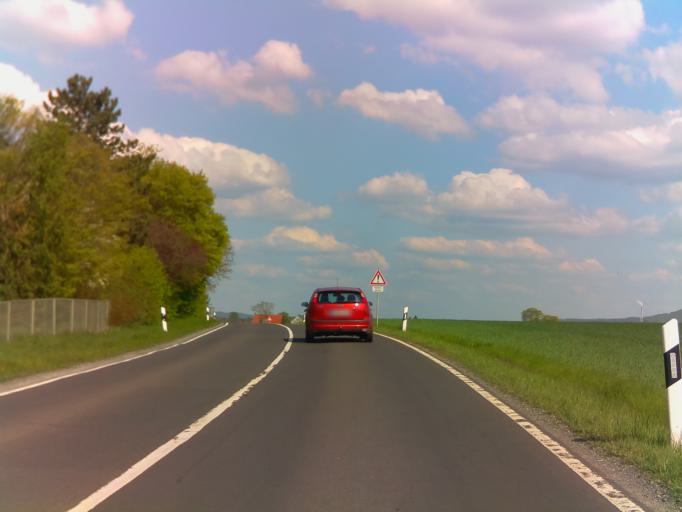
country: DE
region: Bavaria
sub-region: Upper Franconia
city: Meeder
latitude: 50.2971
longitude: 10.9088
